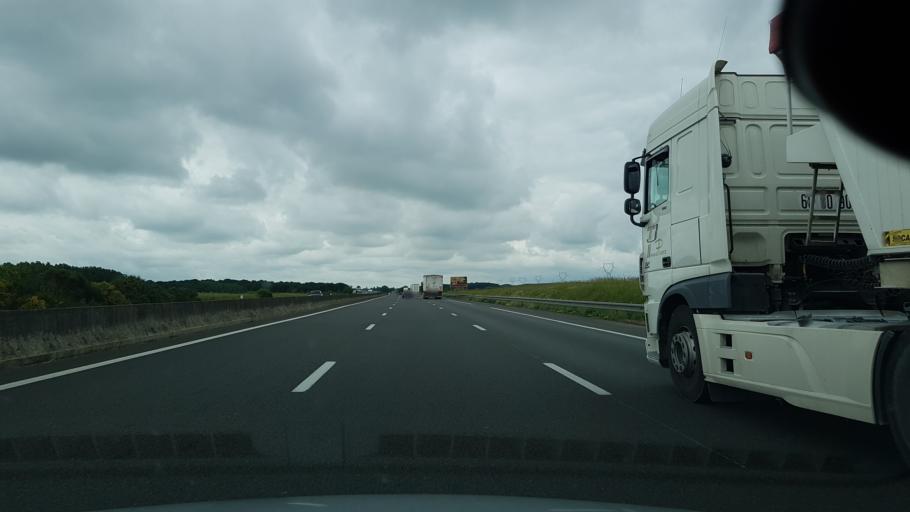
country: FR
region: Centre
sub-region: Departement du Loir-et-Cher
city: Herbault
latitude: 47.6027
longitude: 1.1122
